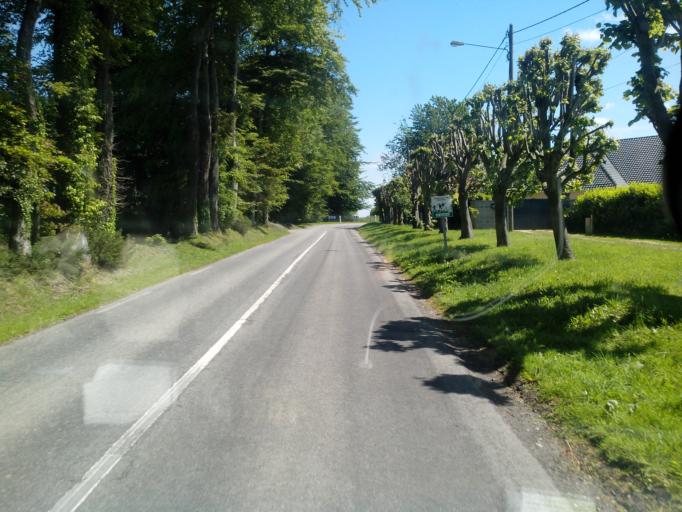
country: FR
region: Haute-Normandie
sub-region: Departement de la Seine-Maritime
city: Turretot
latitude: 49.6221
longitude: 0.2802
